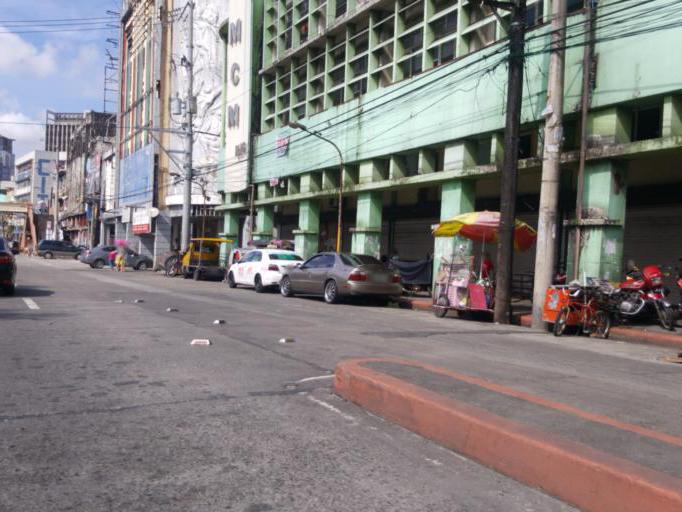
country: PH
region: Metro Manila
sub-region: City of Manila
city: Manila
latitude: 14.6059
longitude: 120.9857
